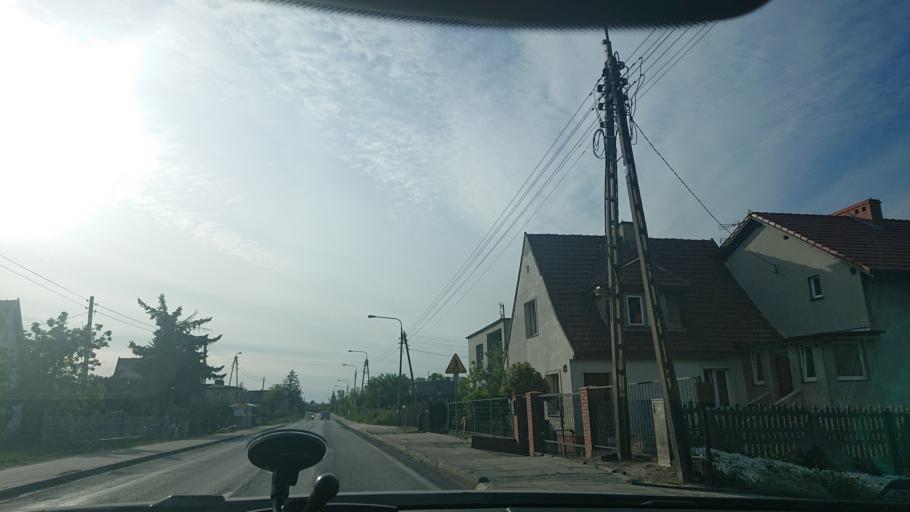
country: PL
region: Greater Poland Voivodeship
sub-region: Powiat gnieznienski
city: Gniezno
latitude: 52.5415
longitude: 17.5786
